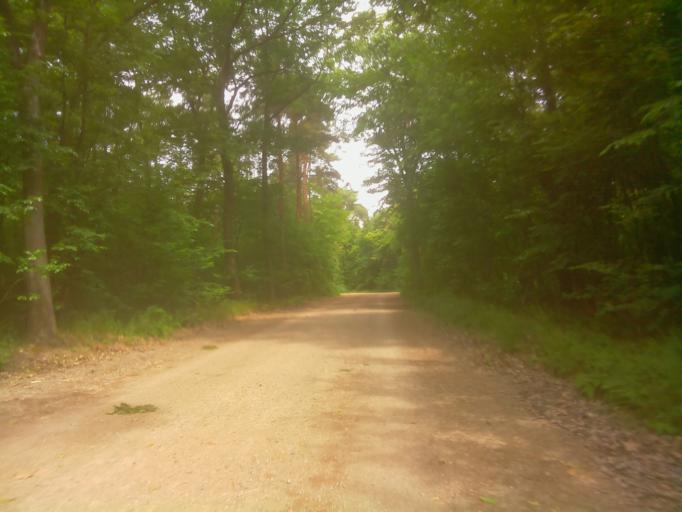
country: DE
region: Baden-Wuerttemberg
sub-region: Karlsruhe Region
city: Mannheim
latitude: 49.5463
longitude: 8.4850
